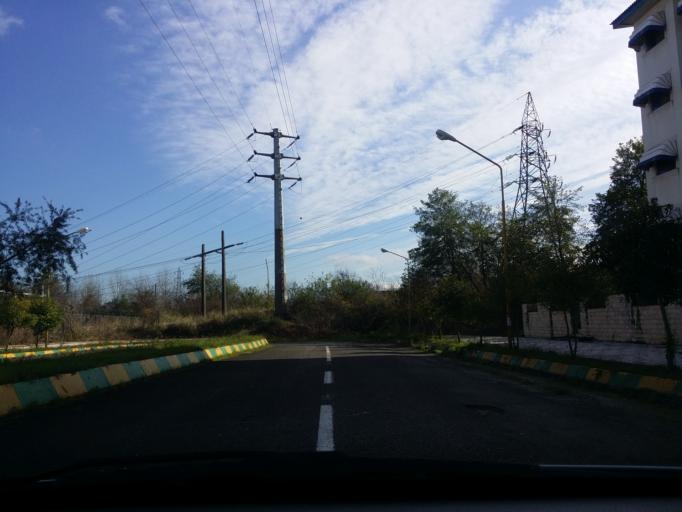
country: IR
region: Mazandaran
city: Chalus
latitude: 36.6740
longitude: 51.3133
